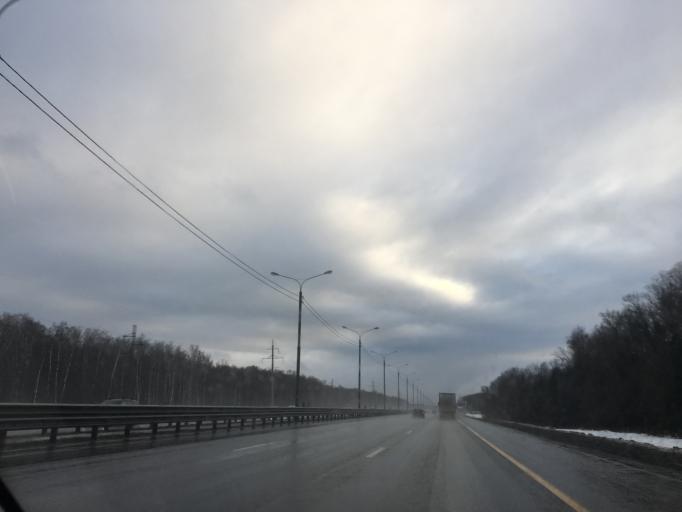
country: RU
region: Moskovskaya
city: Lyubuchany
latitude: 55.2834
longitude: 37.5412
